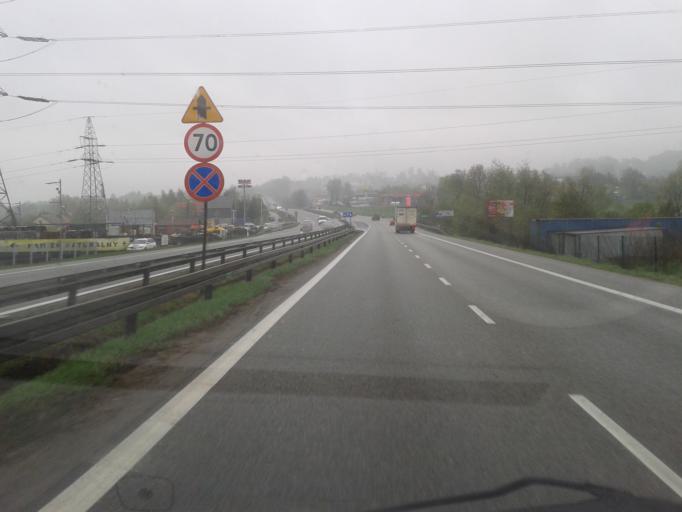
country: PL
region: Lesser Poland Voivodeship
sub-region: Powiat krakowski
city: Mogilany
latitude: 49.9536
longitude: 19.8900
